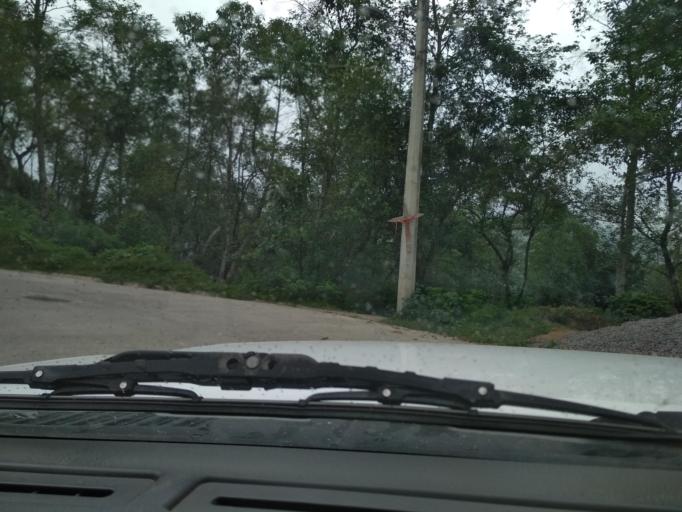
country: MX
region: Veracruz
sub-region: La Perla
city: Chilapa
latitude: 18.9883
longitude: -97.1478
